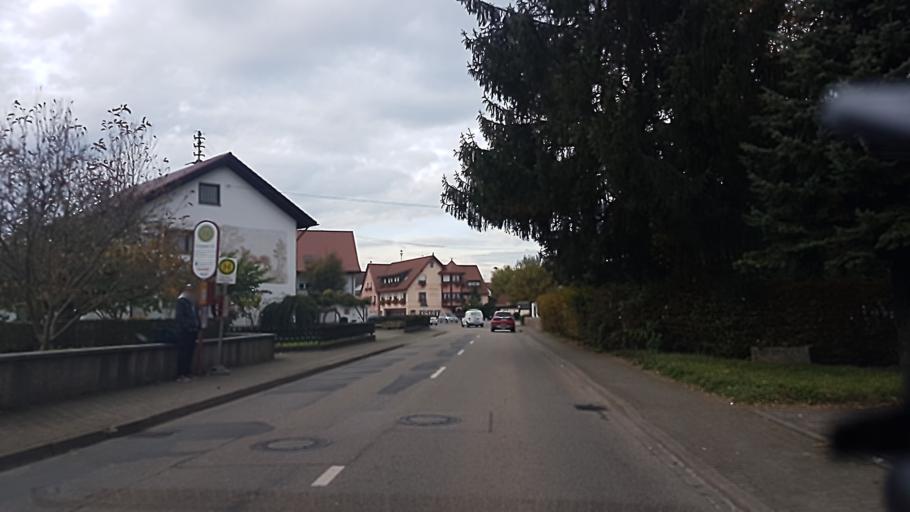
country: DE
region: Baden-Wuerttemberg
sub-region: Freiburg Region
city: Umkirch
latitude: 48.0680
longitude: 7.7727
